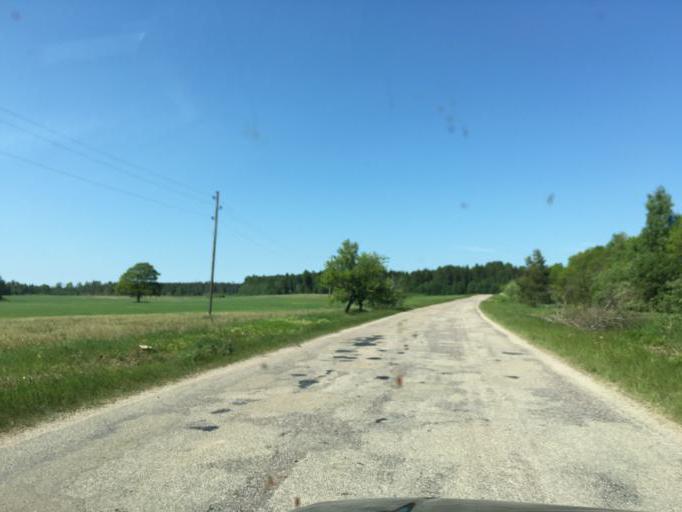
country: LV
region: Dundaga
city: Dundaga
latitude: 57.4706
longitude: 22.3219
